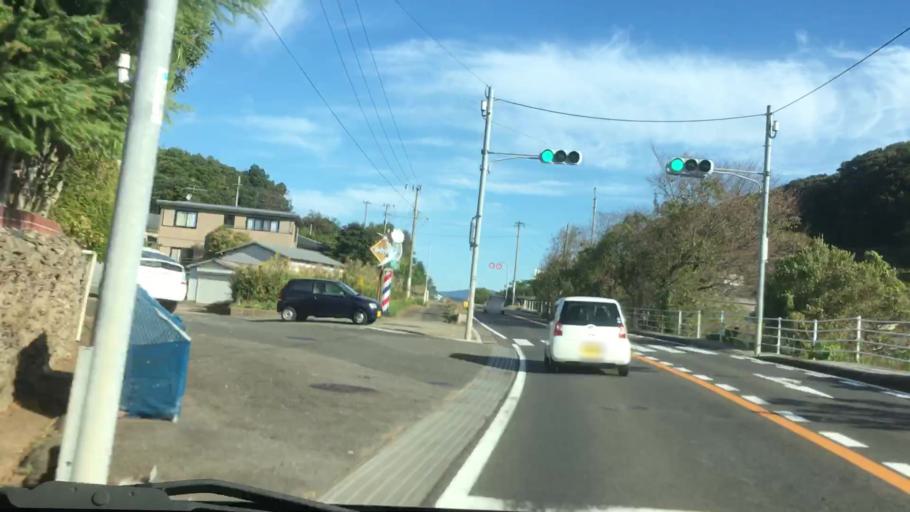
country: JP
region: Nagasaki
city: Sasebo
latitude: 33.0481
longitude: 129.7559
